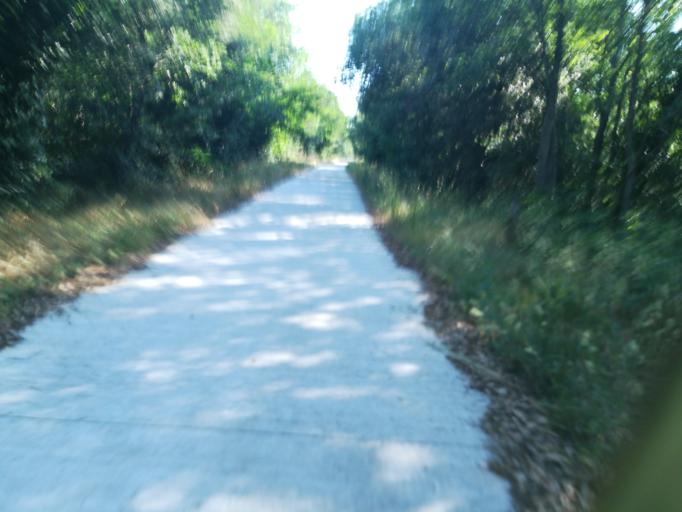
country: FR
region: Languedoc-Roussillon
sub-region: Departement des Pyrenees-Orientales
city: Reiners
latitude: 42.4880
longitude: 2.6992
